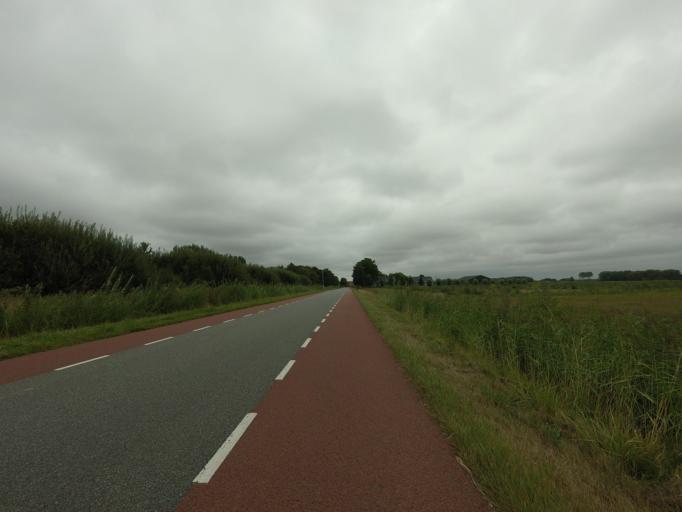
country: NL
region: Gelderland
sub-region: Gemeente Overbetuwe
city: Driel
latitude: 51.9527
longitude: 5.8272
